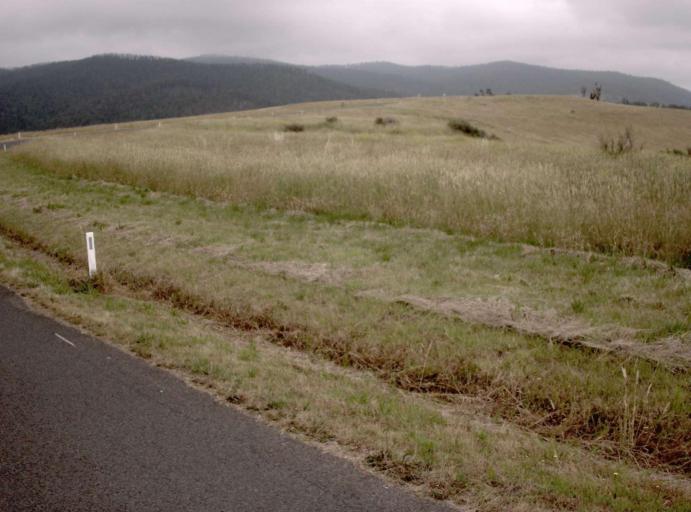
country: AU
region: Victoria
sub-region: Wellington
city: Heyfield
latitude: -37.8393
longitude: 146.6855
